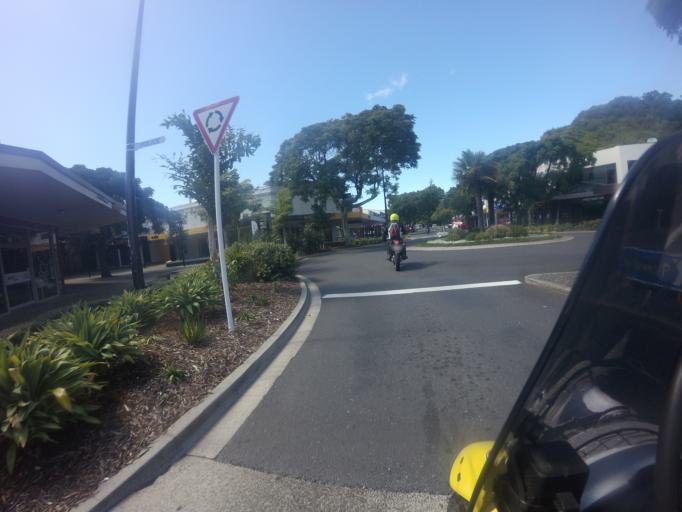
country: NZ
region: Bay of Plenty
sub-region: Whakatane District
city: Whakatane
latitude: -37.9519
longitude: 176.9944
